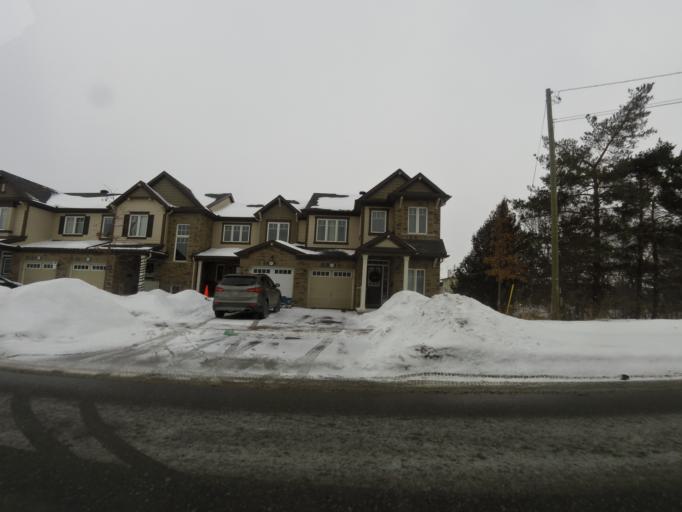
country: CA
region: Ontario
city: Bells Corners
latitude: 45.2854
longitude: -75.9259
